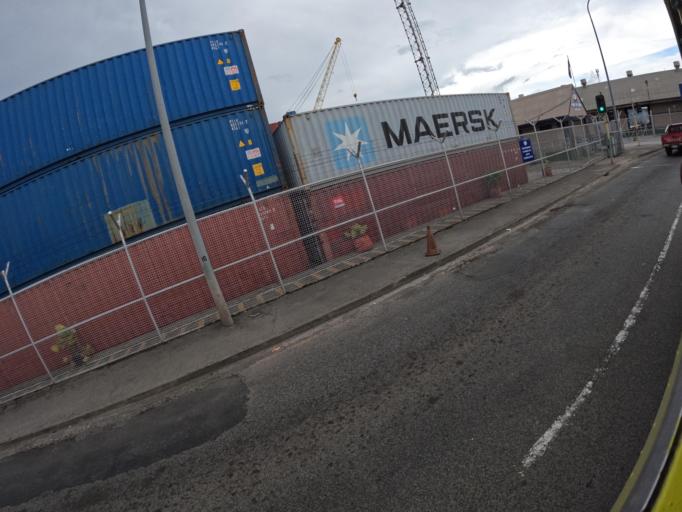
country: FJ
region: Central
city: Suva
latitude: -18.1326
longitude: 178.4255
